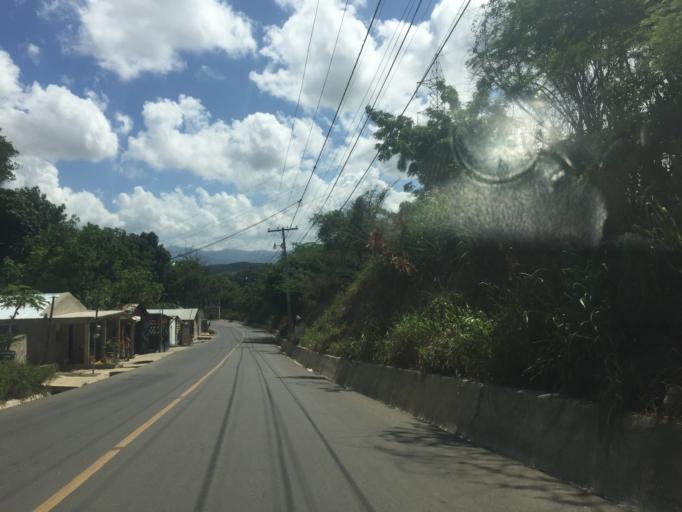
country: DO
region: Santiago
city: Santiago de los Caballeros
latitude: 19.4482
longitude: -70.7544
